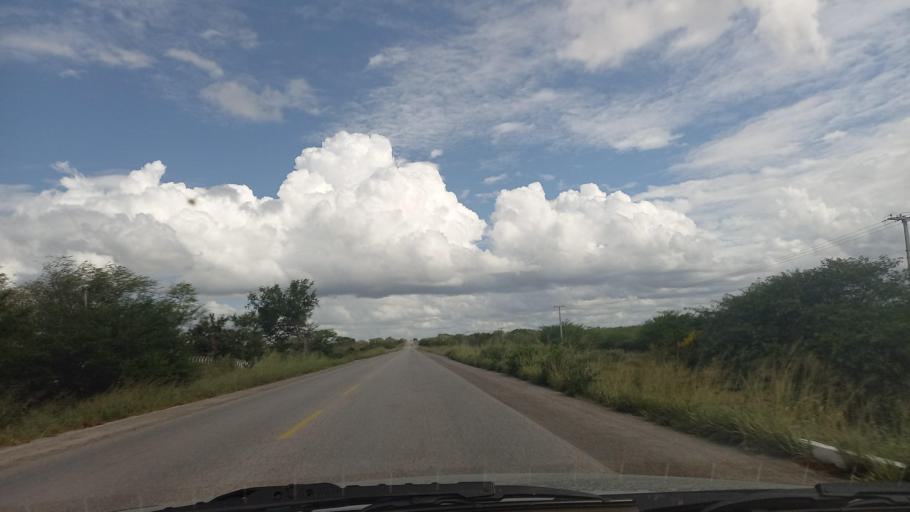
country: BR
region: Pernambuco
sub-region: Cachoeirinha
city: Cachoeirinha
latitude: -8.4507
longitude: -36.2112
